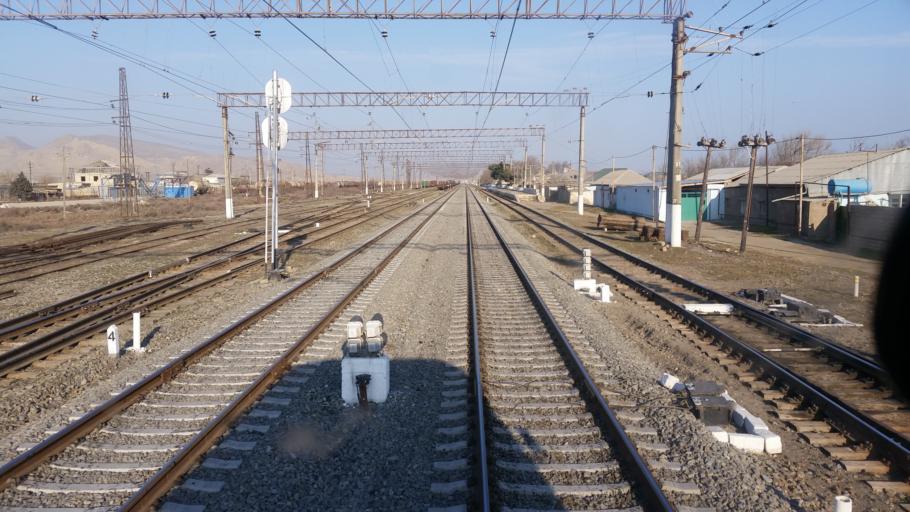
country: AZ
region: Baki
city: Korgoz
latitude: 40.2394
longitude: 49.5919
